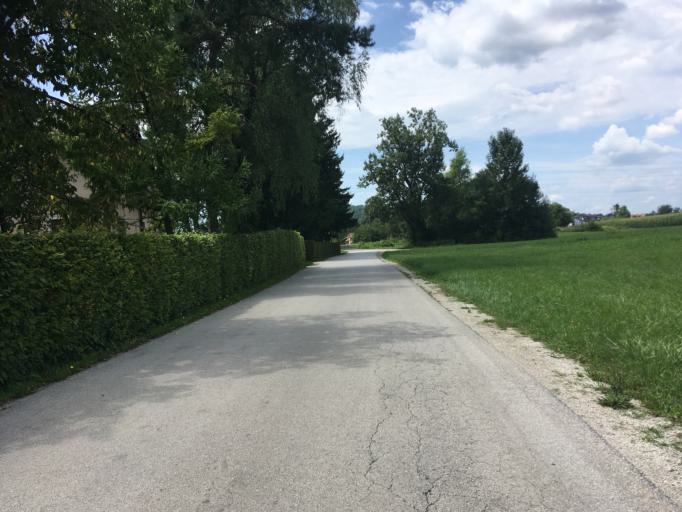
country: SI
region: Menges
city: Menges
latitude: 46.1630
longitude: 14.5850
